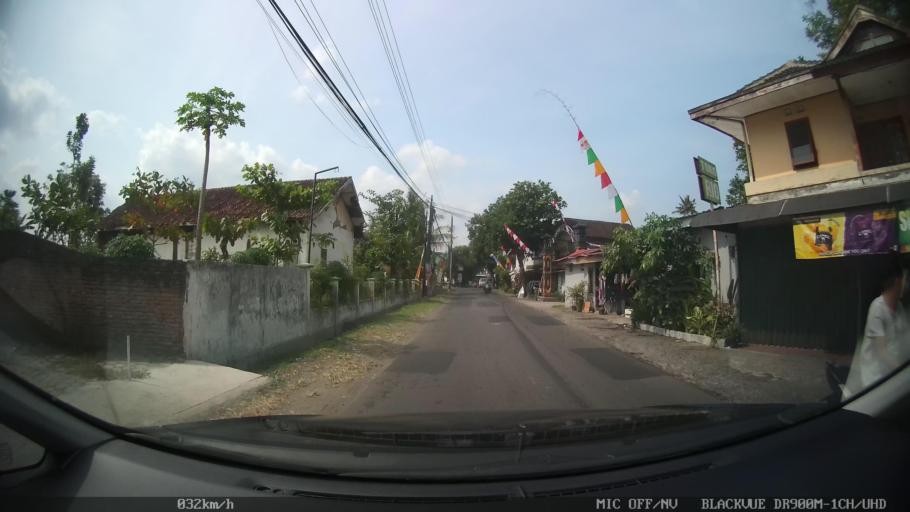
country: ID
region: Daerah Istimewa Yogyakarta
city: Depok
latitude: -7.7888
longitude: 110.4475
